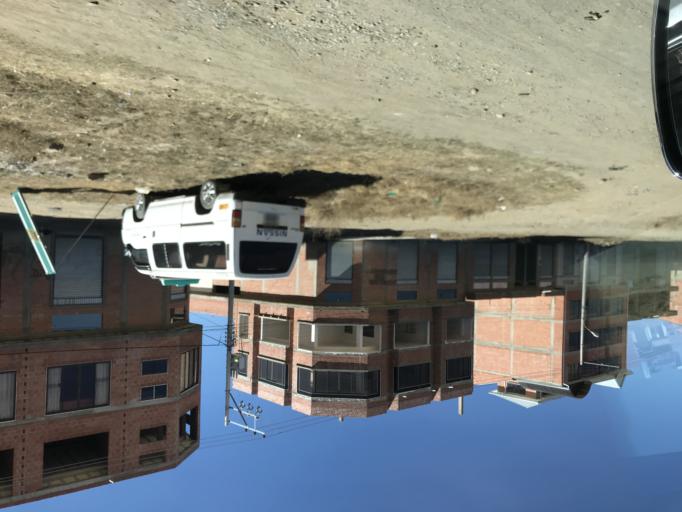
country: BO
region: La Paz
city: La Paz
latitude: -16.5076
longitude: -68.2608
